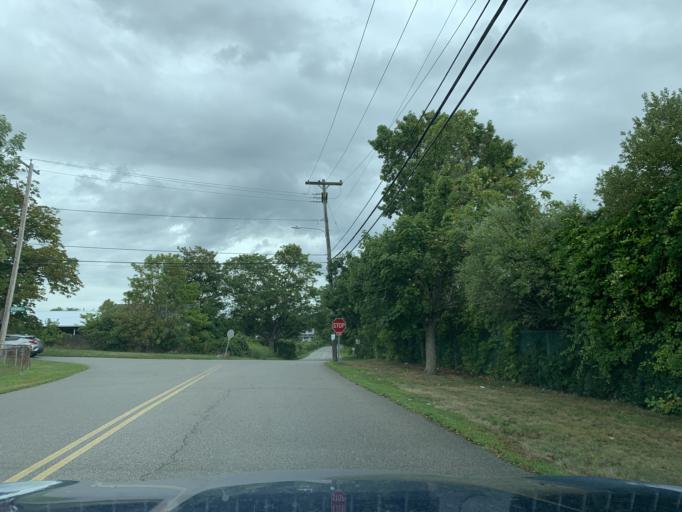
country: US
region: Rhode Island
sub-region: Bristol County
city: Warren
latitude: 41.7305
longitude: -71.2657
